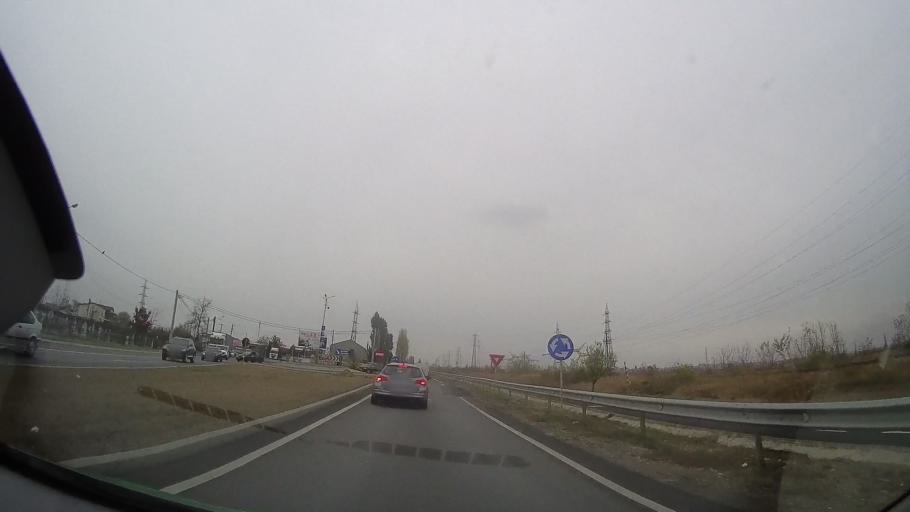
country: RO
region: Prahova
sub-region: Comuna Blejoiu
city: Ploiestiori
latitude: 44.9757
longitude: 26.0176
